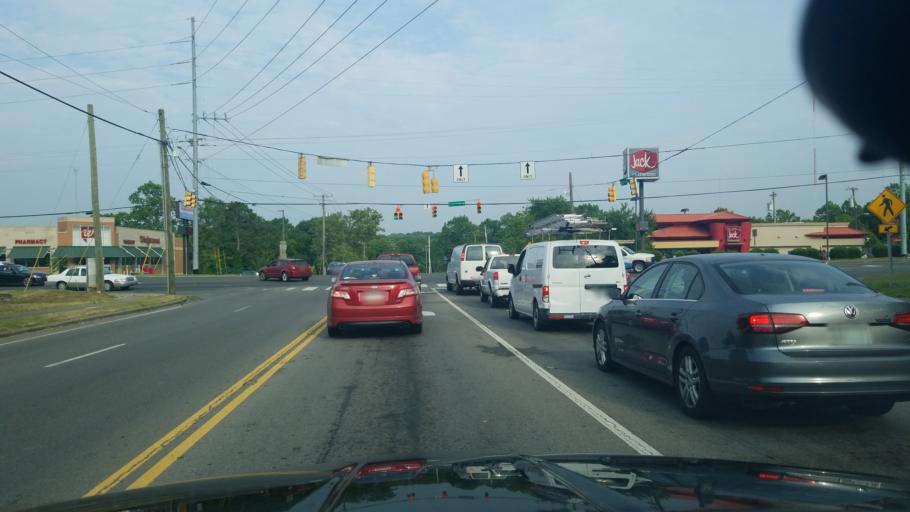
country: US
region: Tennessee
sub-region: Davidson County
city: Goodlettsville
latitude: 36.2691
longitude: -86.7552
